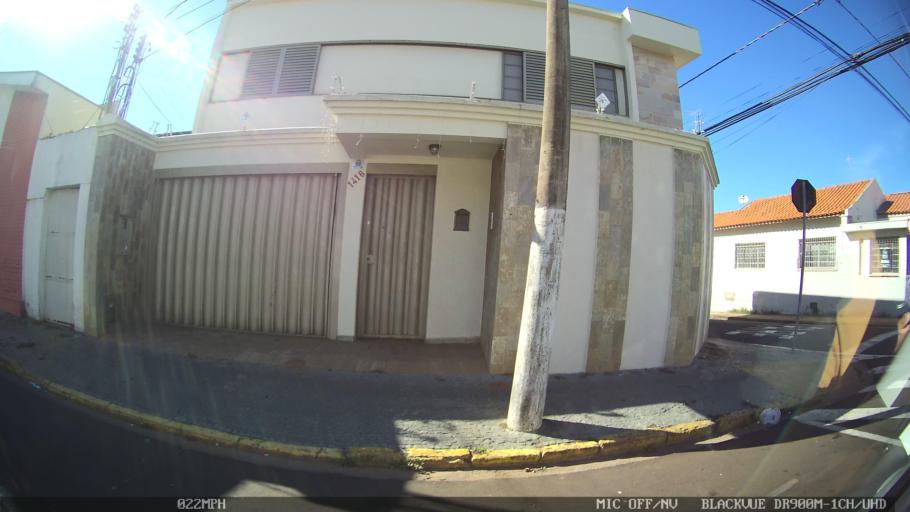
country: BR
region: Sao Paulo
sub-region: Franca
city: Franca
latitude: -20.5420
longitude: -47.4001
